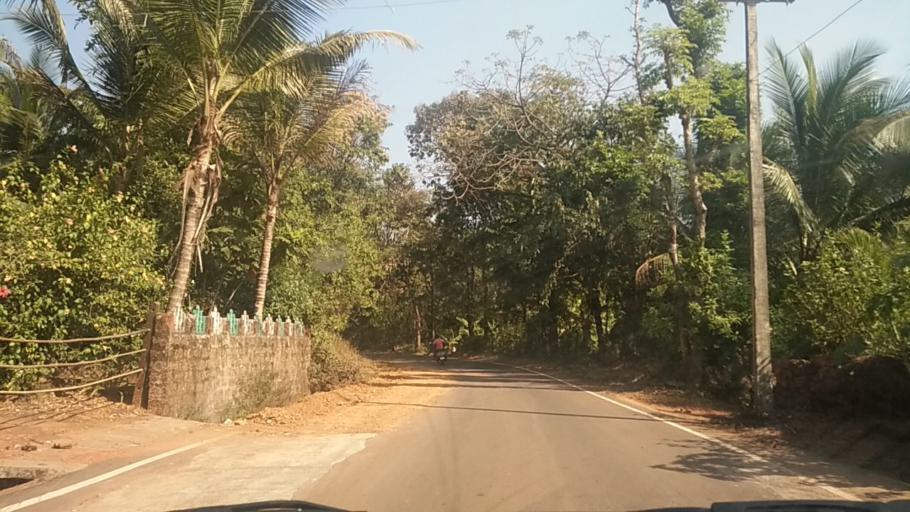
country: IN
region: Goa
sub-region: South Goa
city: Sanguem
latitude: 15.1899
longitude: 74.2276
